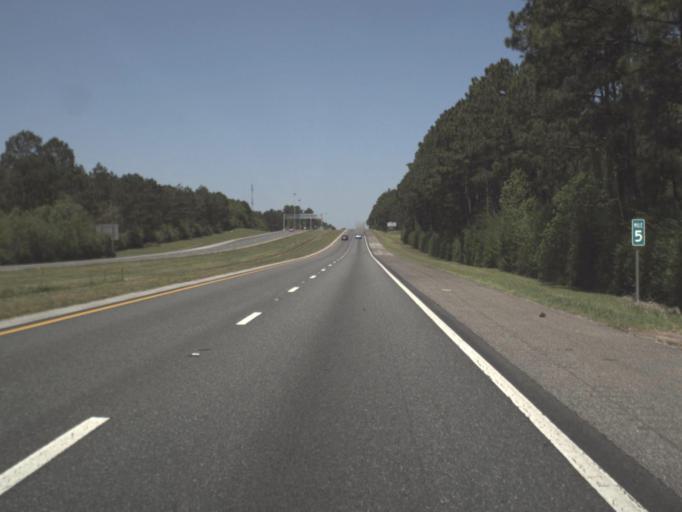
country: US
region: Florida
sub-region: Escambia County
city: Gonzalez
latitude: 30.5393
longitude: -87.3412
